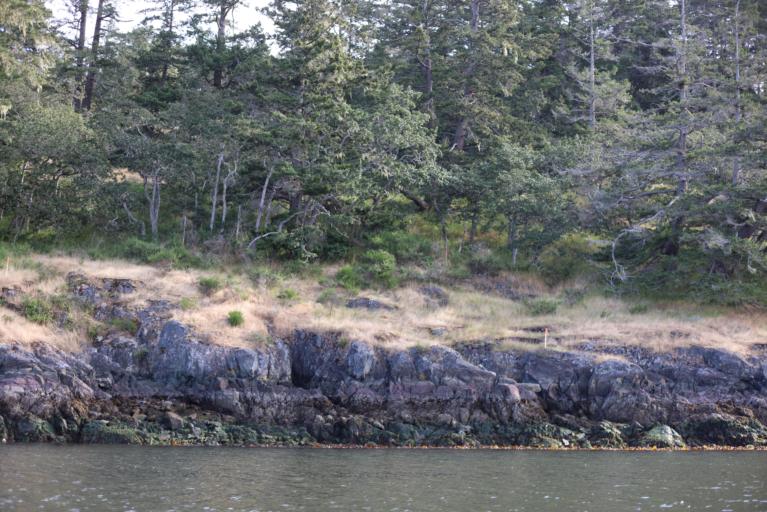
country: CA
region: British Columbia
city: Metchosin
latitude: 48.3445
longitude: -123.5609
